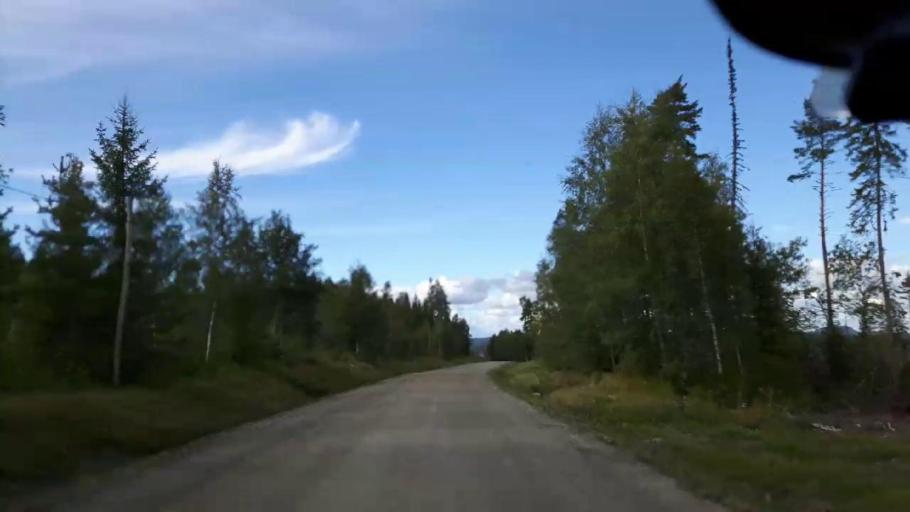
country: SE
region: Jaemtland
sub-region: Ragunda Kommun
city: Hammarstrand
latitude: 63.1353
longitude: 15.9468
